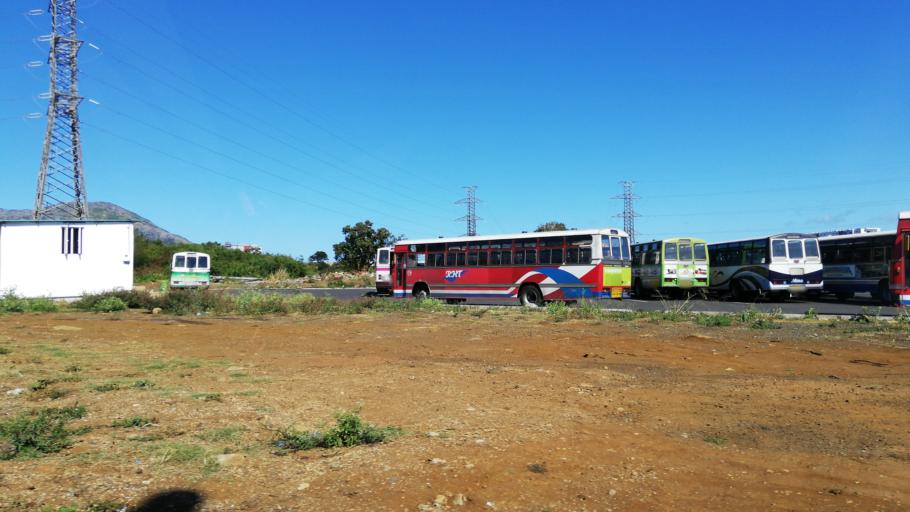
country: MU
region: Plaines Wilhems
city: Ebene
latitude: -20.2404
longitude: 57.4807
